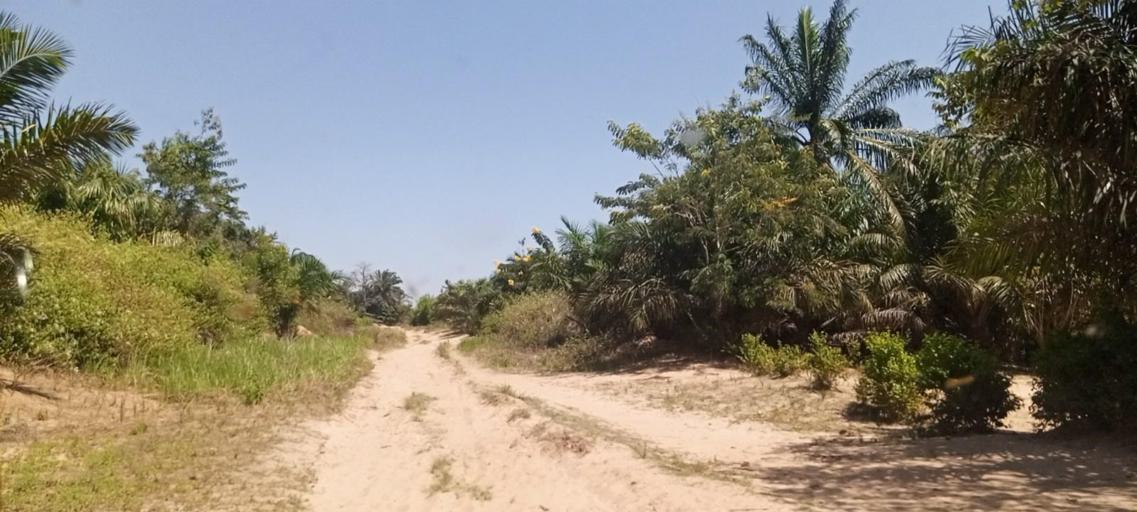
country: CD
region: Kasai-Oriental
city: Kabinda
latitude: -5.9535
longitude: 24.8032
